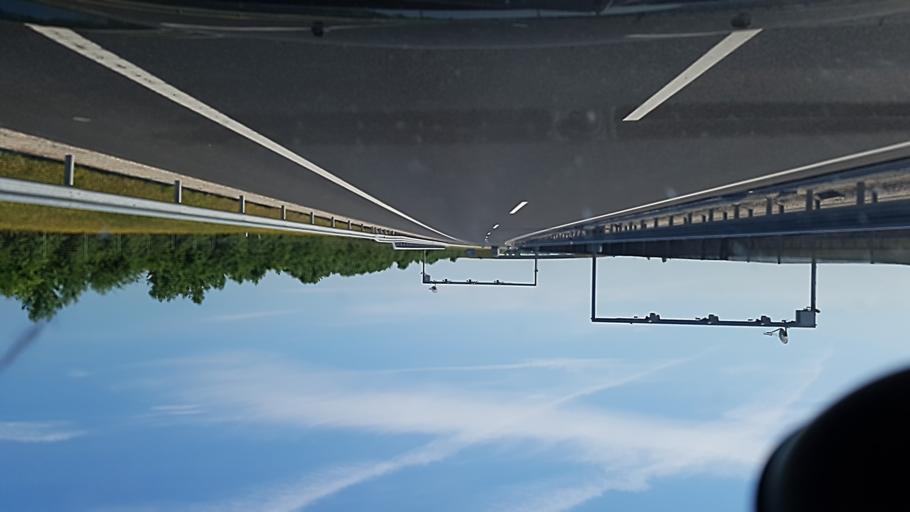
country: HU
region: Tolna
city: Szedres
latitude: 46.4465
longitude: 18.7061
